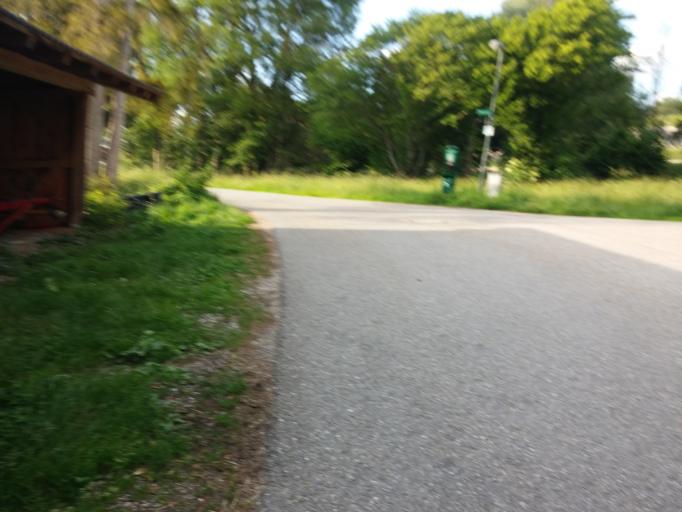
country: DE
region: Bavaria
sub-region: Upper Bavaria
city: Grafing bei Munchen
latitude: 48.0366
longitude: 11.9741
